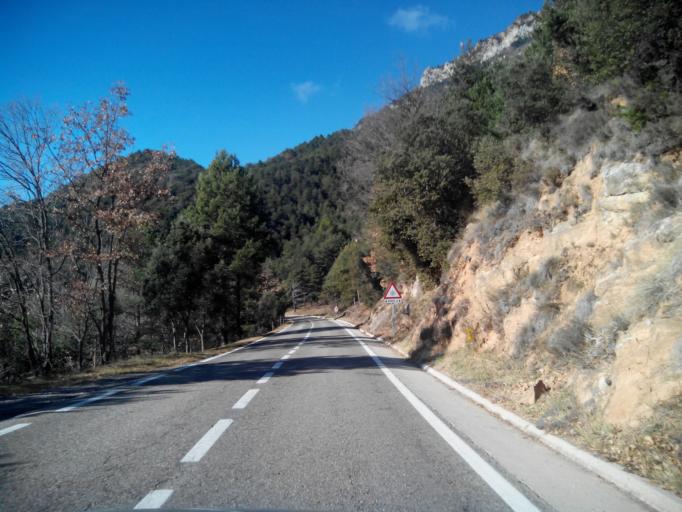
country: ES
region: Catalonia
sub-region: Provincia de Barcelona
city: Castellar del Riu
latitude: 42.0964
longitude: 1.7954
